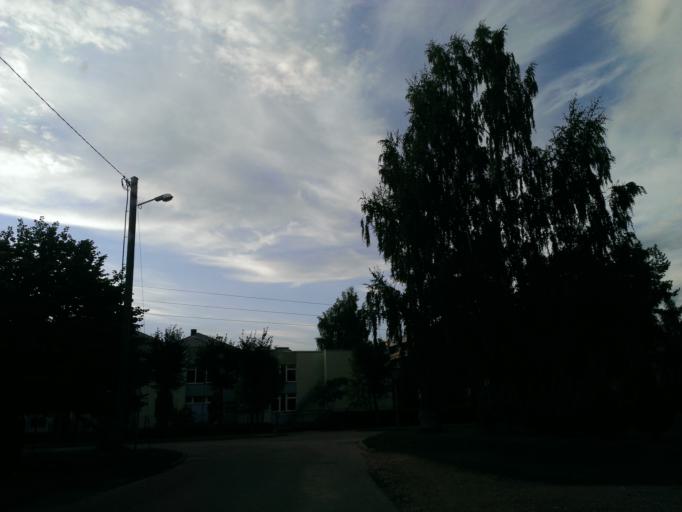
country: LV
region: Ikskile
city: Ikskile
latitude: 56.8378
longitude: 24.5025
